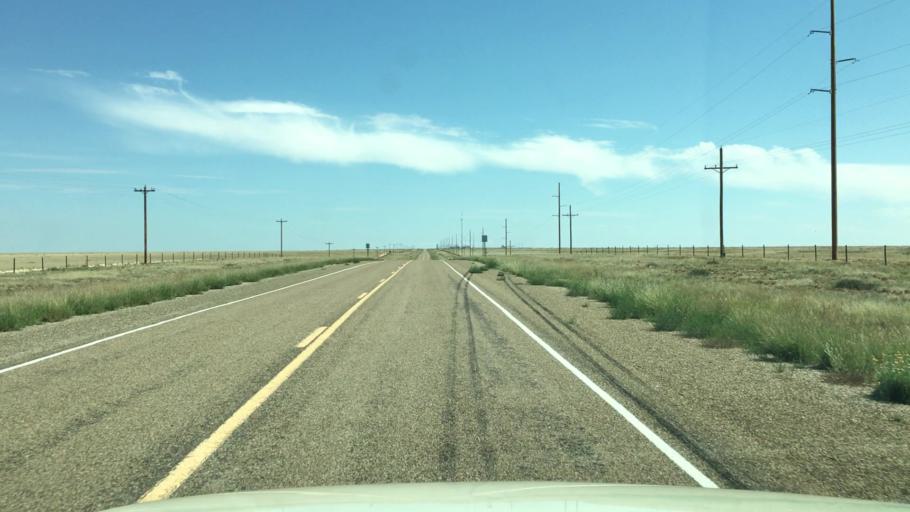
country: US
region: New Mexico
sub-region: Chaves County
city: Roswell
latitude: 33.9456
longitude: -104.5904
